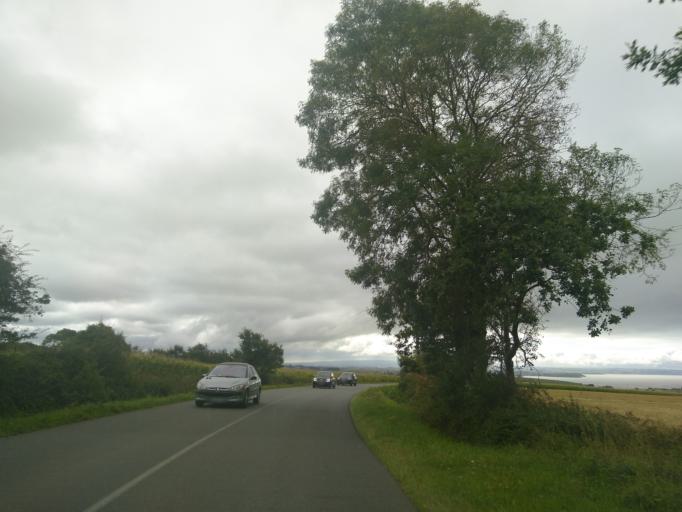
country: FR
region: Brittany
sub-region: Departement du Finistere
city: Telgruc-sur-Mer
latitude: 48.2231
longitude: -4.3246
